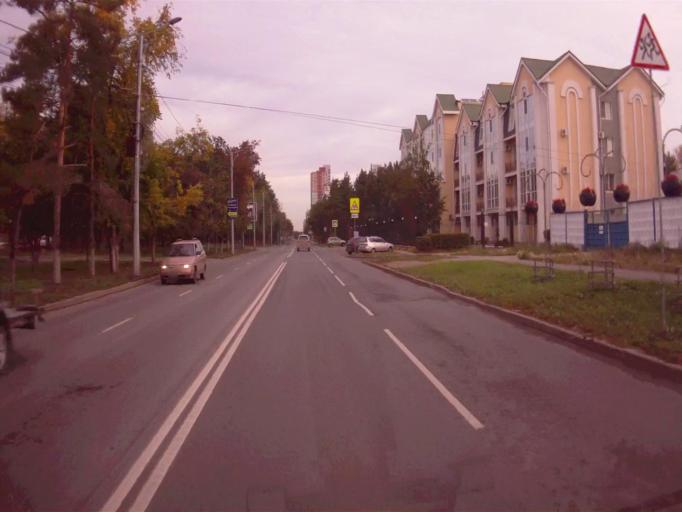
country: RU
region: Chelyabinsk
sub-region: Gorod Chelyabinsk
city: Chelyabinsk
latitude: 55.1502
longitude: 61.3652
